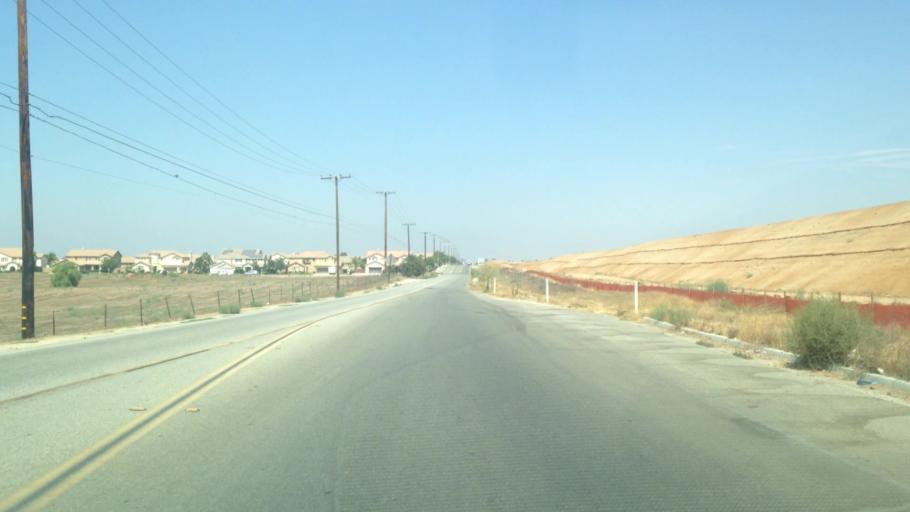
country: US
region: California
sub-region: Riverside County
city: Mead Valley
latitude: 33.8735
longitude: -117.3139
